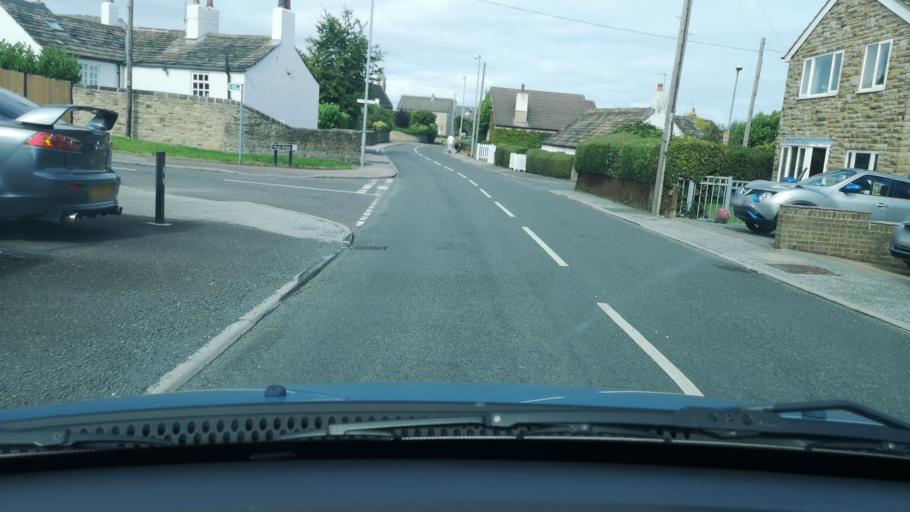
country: GB
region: England
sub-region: City and Borough of Wakefield
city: Horbury
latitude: 53.6481
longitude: -1.5716
